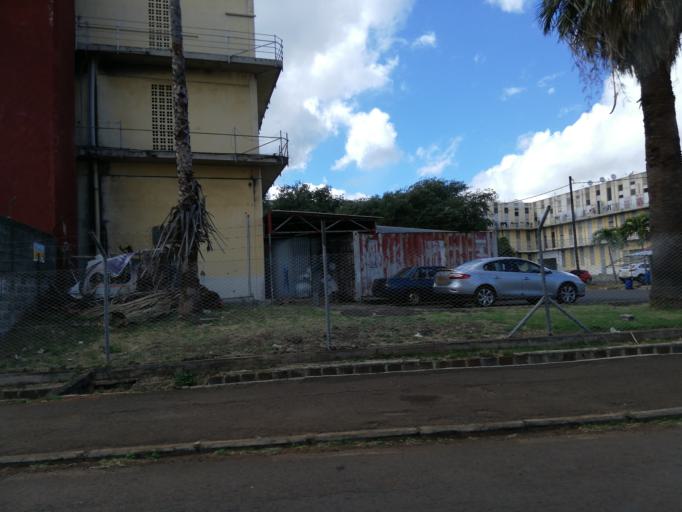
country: MU
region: Black River
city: Petite Riviere
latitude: -20.1907
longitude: 57.4659
